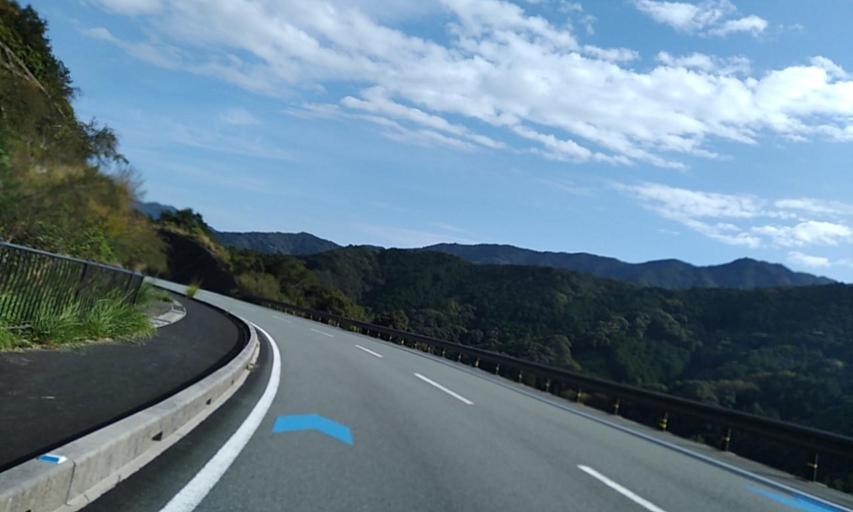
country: JP
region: Mie
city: Owase
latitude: 34.2513
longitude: 136.4312
